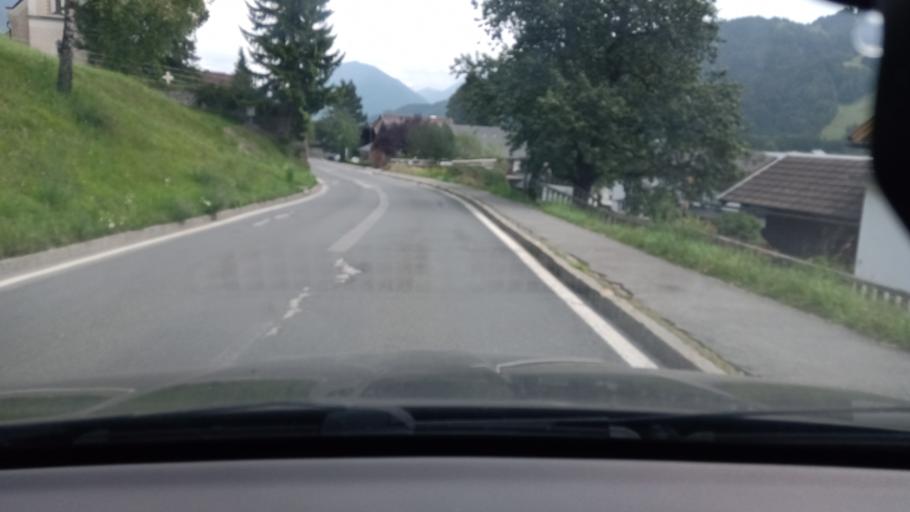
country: AT
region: Carinthia
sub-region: Politischer Bezirk Spittal an der Drau
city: Steinfeld
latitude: 46.7184
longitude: 13.2887
